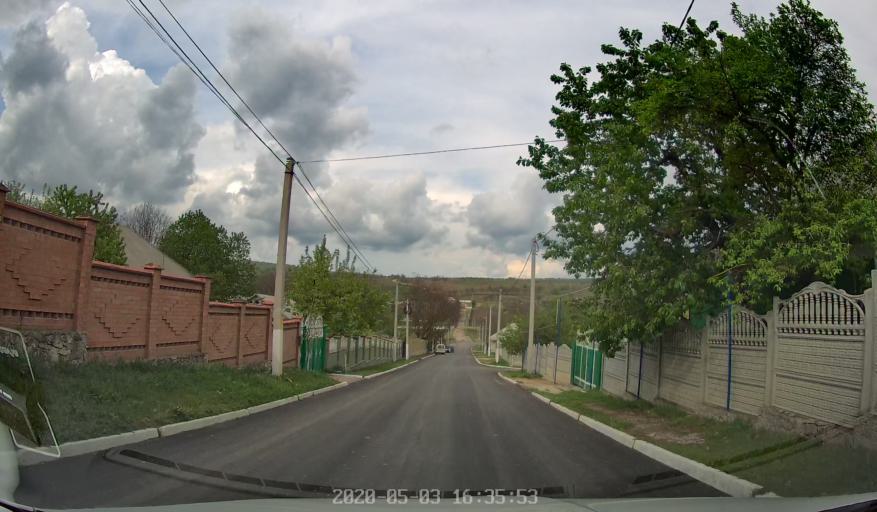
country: MD
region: Calarasi
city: Calarasi
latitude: 47.1923
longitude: 28.3571
